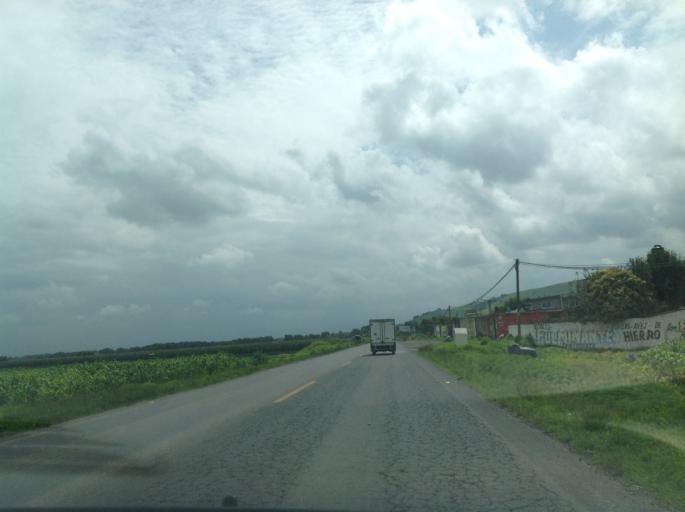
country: MX
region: Morelos
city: Tenango de Arista
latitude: 19.1069
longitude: -99.5768
